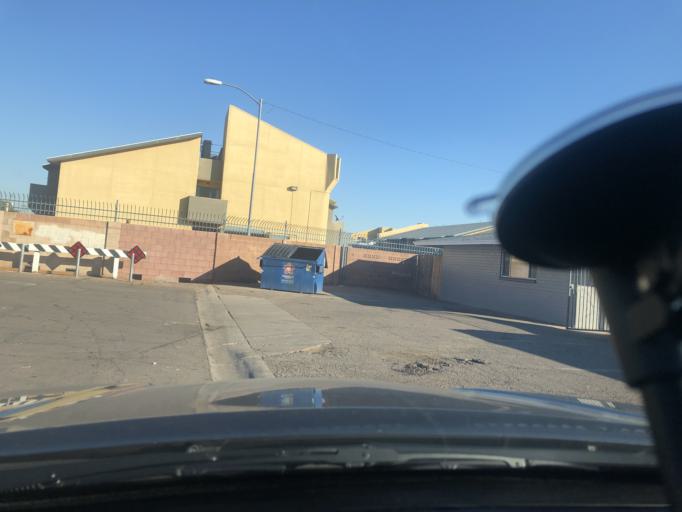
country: US
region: Arizona
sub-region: Maricopa County
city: Phoenix
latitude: 33.4568
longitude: -112.0343
